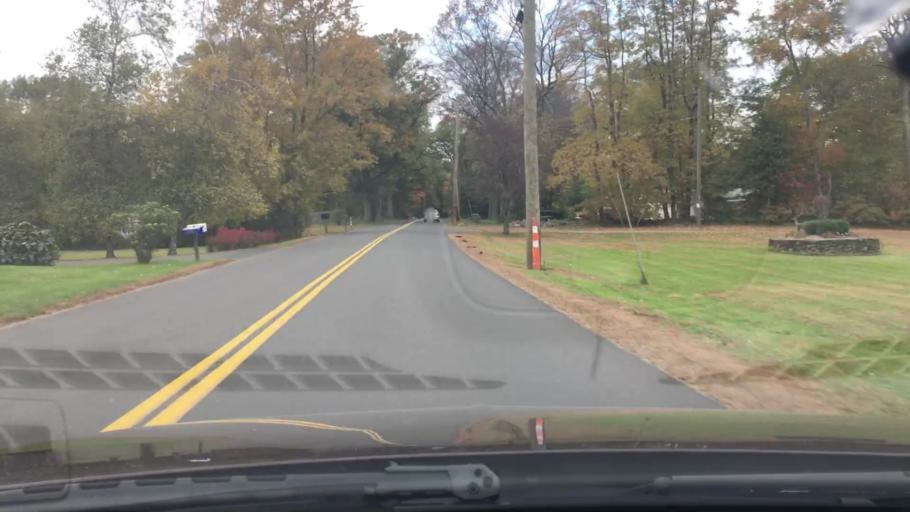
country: US
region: Connecticut
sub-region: Tolland County
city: Ellington
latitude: 41.9463
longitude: -72.4813
